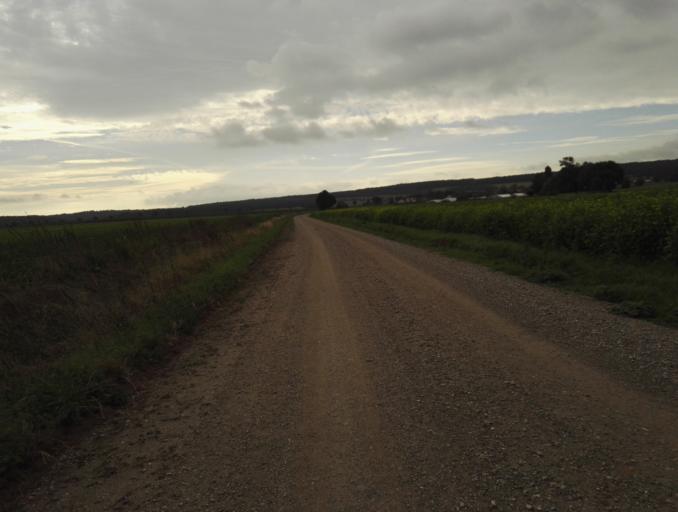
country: DE
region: Lower Saxony
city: Schellerten
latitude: 52.1455
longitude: 10.0610
